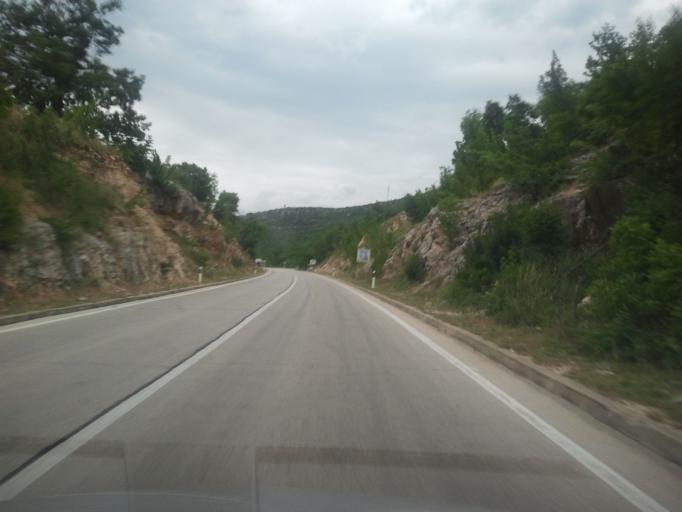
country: HR
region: Zadarska
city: Krusevo
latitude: 44.1633
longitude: 15.6265
